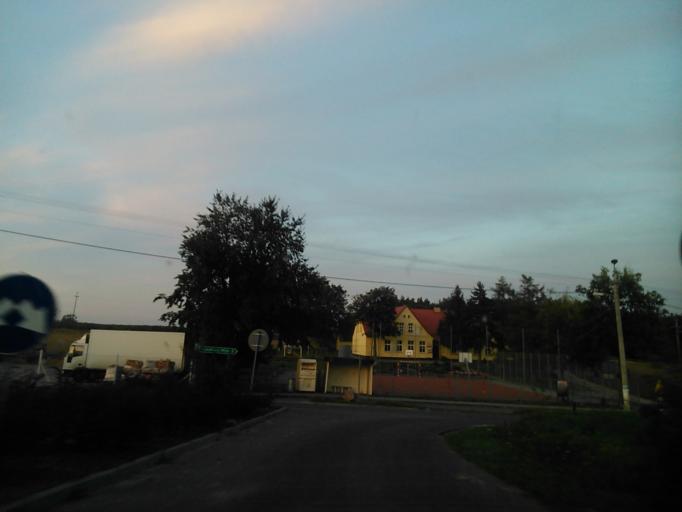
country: PL
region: Kujawsko-Pomorskie
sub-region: Powiat golubsko-dobrzynski
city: Golub-Dobrzyn
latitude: 53.1342
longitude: 19.0741
